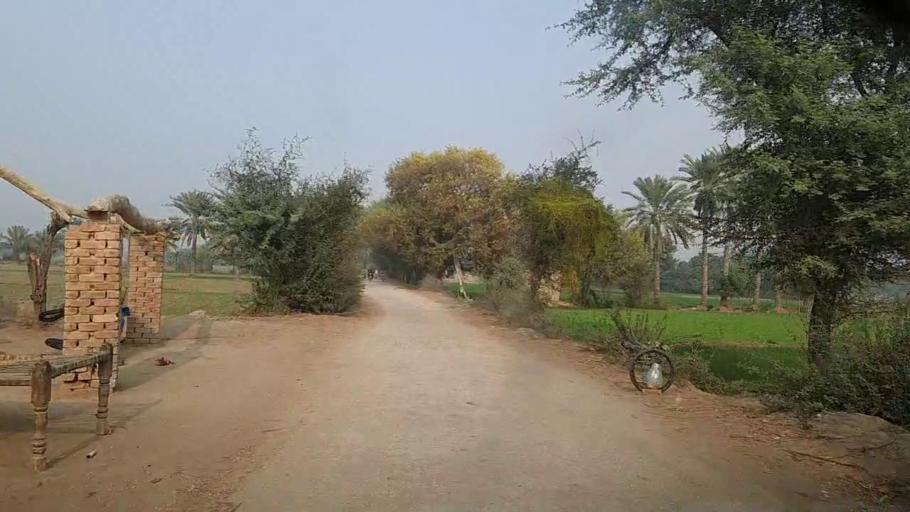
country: PK
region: Sindh
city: Bozdar
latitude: 27.1331
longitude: 68.6590
